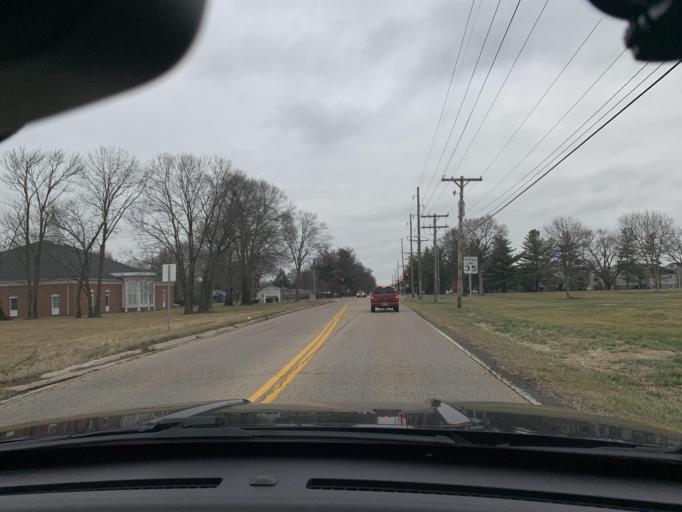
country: US
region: Illinois
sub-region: Sangamon County
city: Jerome
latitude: 39.7557
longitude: -89.6866
